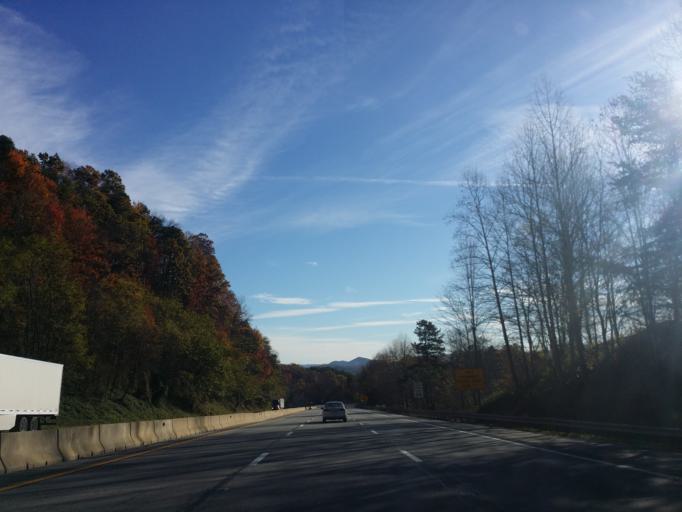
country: US
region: North Carolina
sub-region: Buncombe County
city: Black Mountain
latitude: 35.6250
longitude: -82.2130
